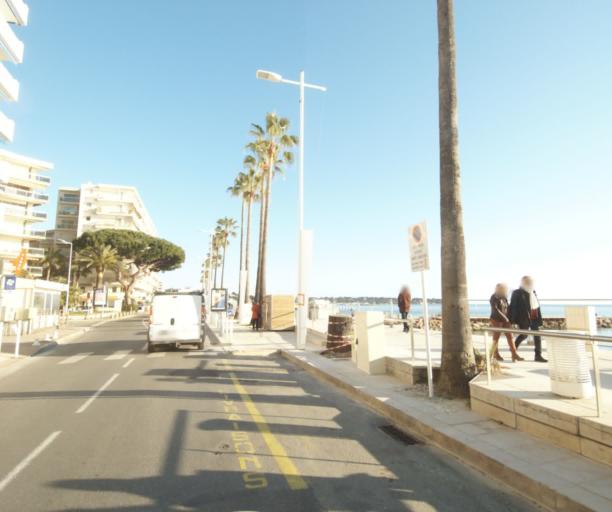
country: FR
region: Provence-Alpes-Cote d'Azur
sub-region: Departement des Alpes-Maritimes
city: Antibes
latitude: 43.5698
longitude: 7.1063
